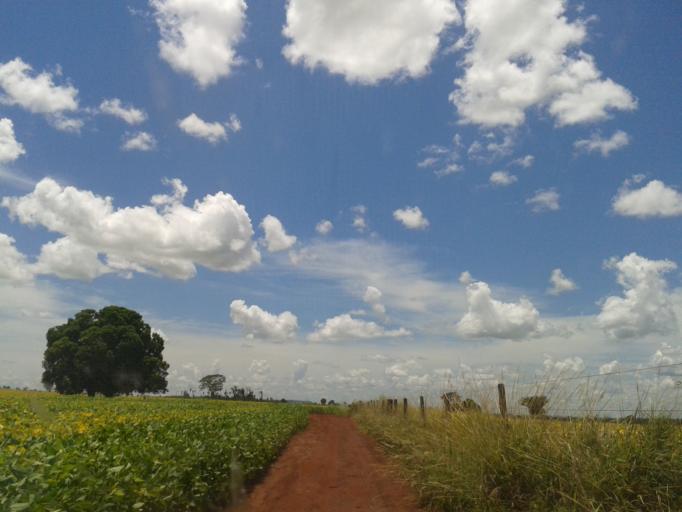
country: BR
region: Minas Gerais
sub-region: Capinopolis
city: Capinopolis
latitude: -18.7705
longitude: -49.7927
